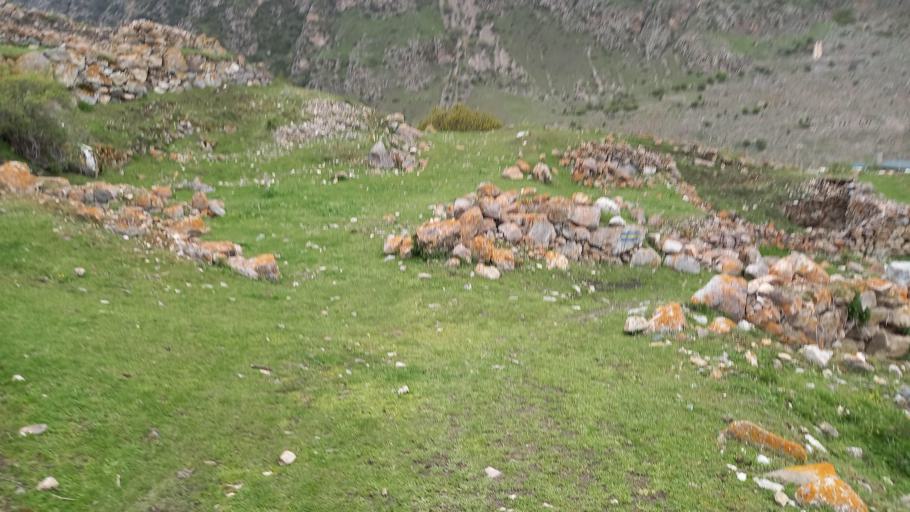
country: RU
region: Kabardino-Balkariya
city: Verkhnyaya Balkariya
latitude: 43.1017
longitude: 43.4359
